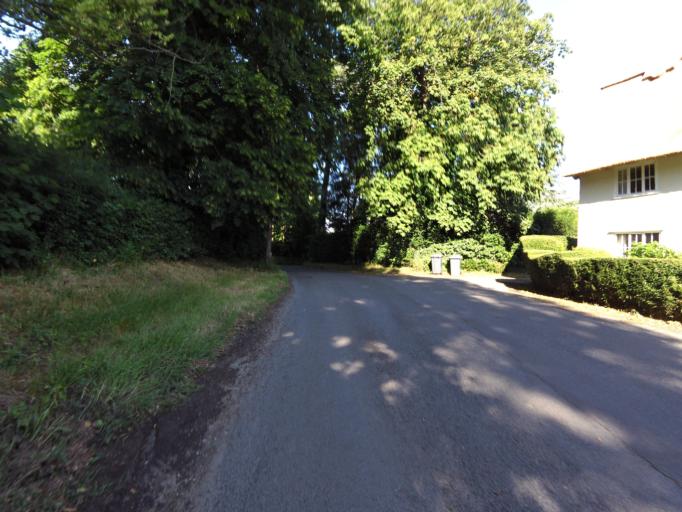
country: GB
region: England
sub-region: Suffolk
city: Leiston
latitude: 52.2737
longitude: 1.5473
